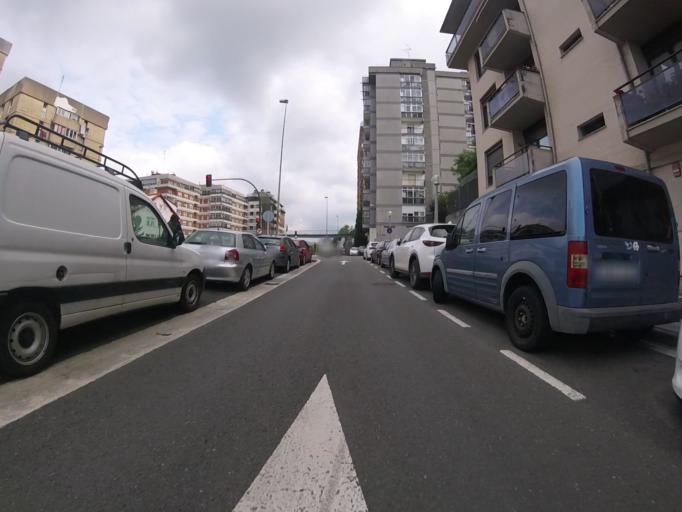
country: ES
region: Basque Country
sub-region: Provincia de Guipuzcoa
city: San Sebastian
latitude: 43.3091
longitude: -1.9674
